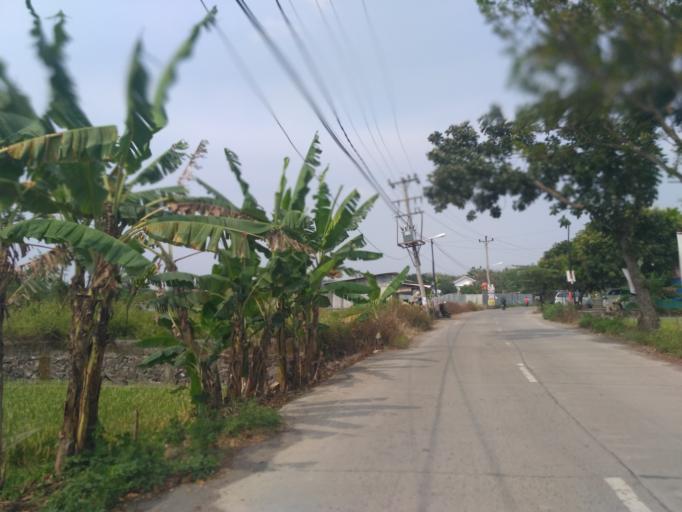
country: ID
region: Central Java
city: Mranggen
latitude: -7.0586
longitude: 110.4727
